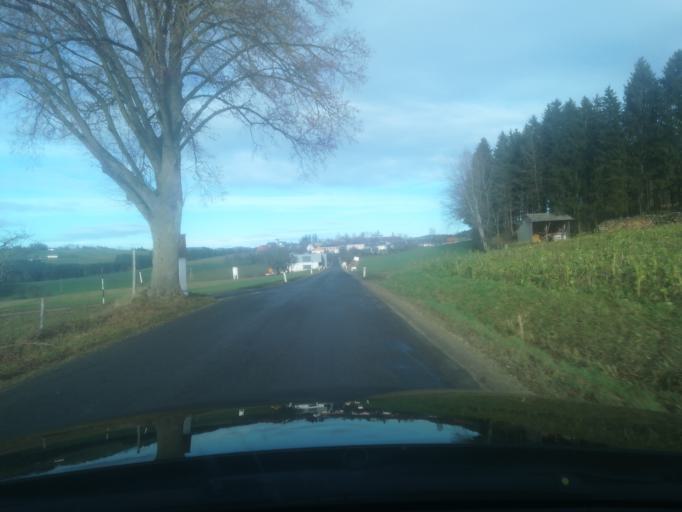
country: AT
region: Upper Austria
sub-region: Politischer Bezirk Perg
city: Perg
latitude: 48.3642
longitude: 14.6319
